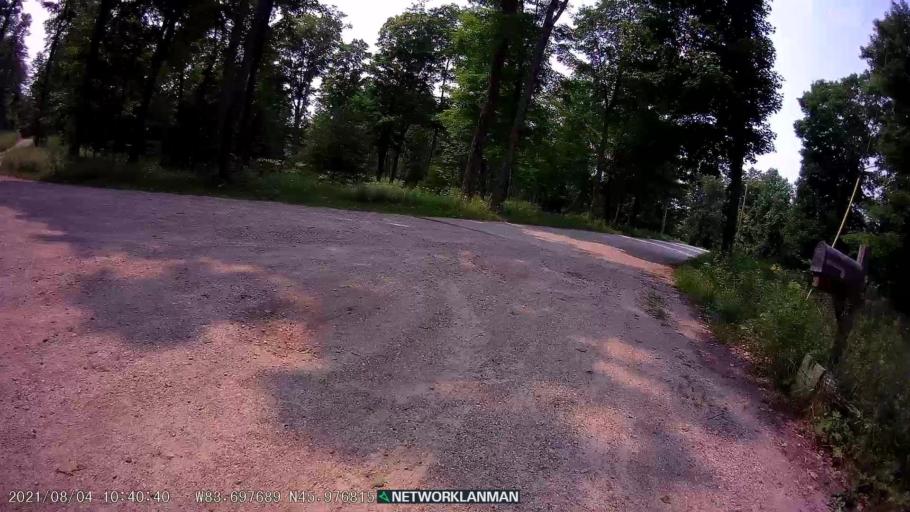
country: CA
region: Ontario
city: Thessalon
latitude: 45.9768
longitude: -83.6980
